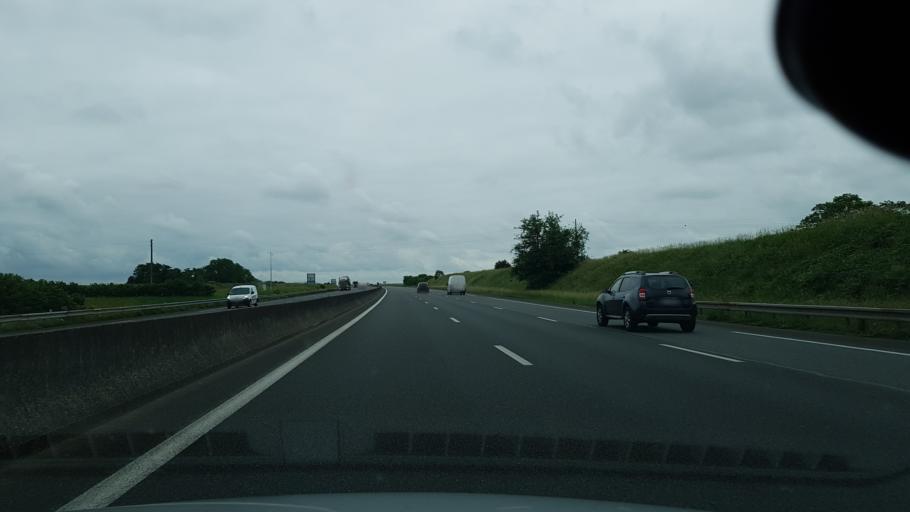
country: FR
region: Centre
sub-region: Departement du Loir-et-Cher
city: La Chaussee-Saint-Victor
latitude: 47.6469
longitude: 1.3679
